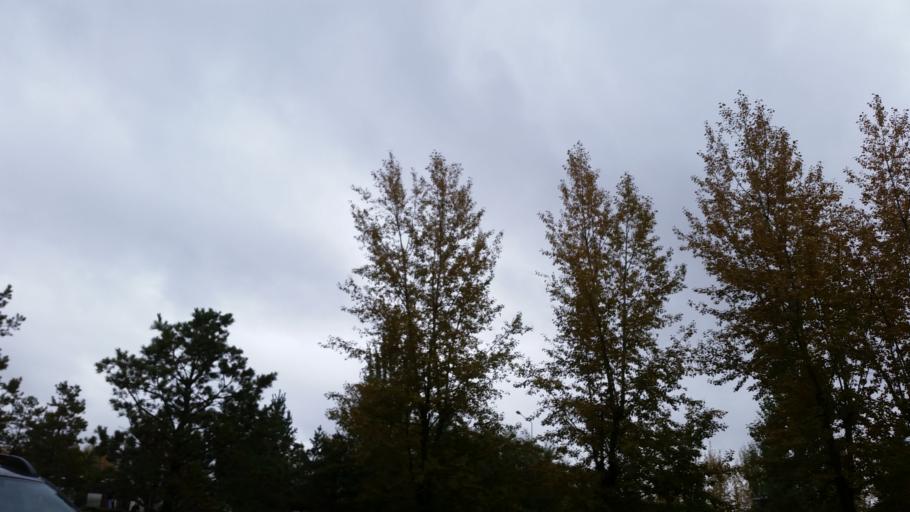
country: KZ
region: Astana Qalasy
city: Astana
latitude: 51.1509
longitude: 71.4979
